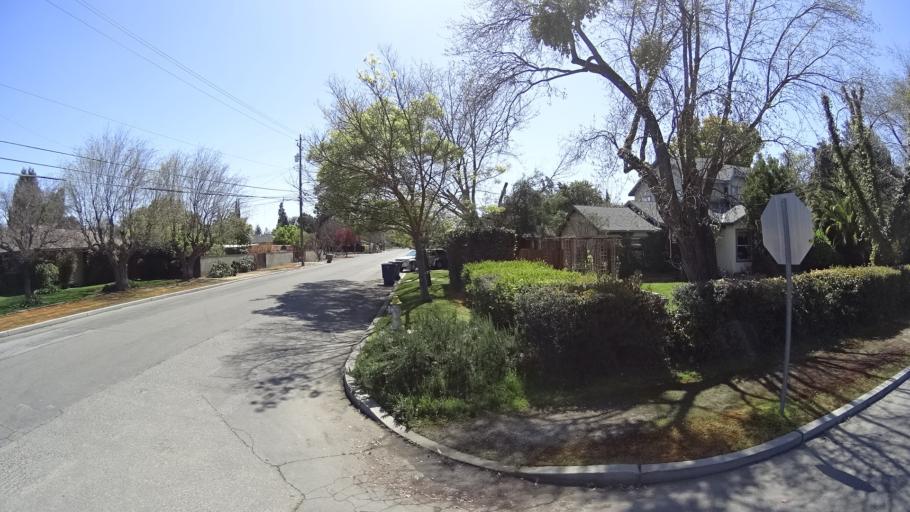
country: US
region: California
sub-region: Fresno County
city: Fresno
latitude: 36.8056
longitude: -119.8243
